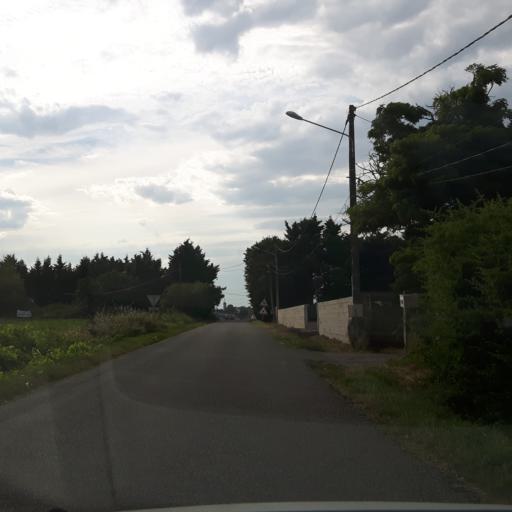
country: FR
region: Midi-Pyrenees
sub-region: Departement de la Haute-Garonne
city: Castelnau-d'Estretefonds
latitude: 43.7962
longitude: 1.3591
